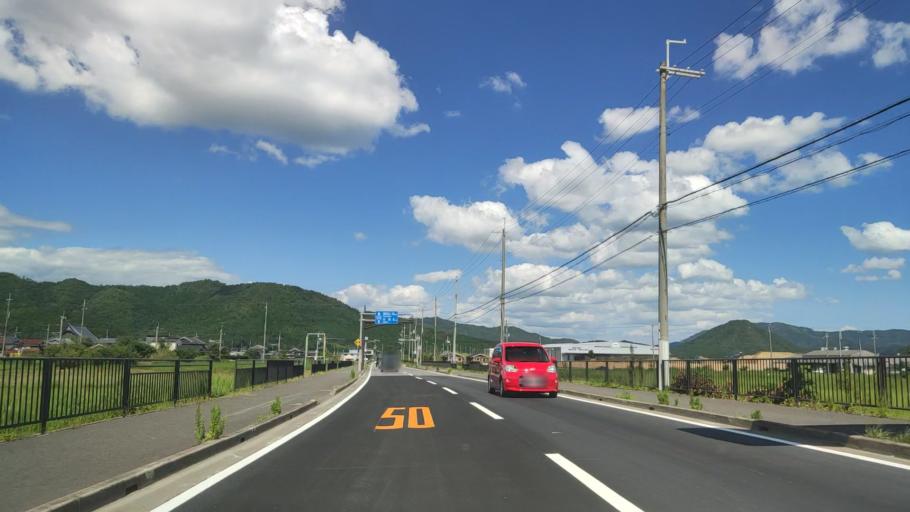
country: JP
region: Kyoto
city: Fukuchiyama
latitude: 35.1681
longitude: 135.1176
